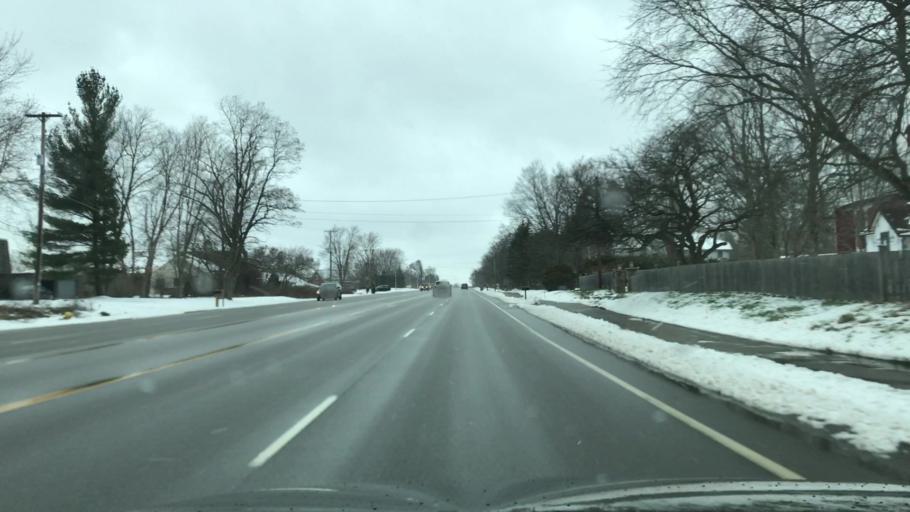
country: US
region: Michigan
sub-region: Kent County
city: Forest Hills
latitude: 42.9354
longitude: -85.5286
